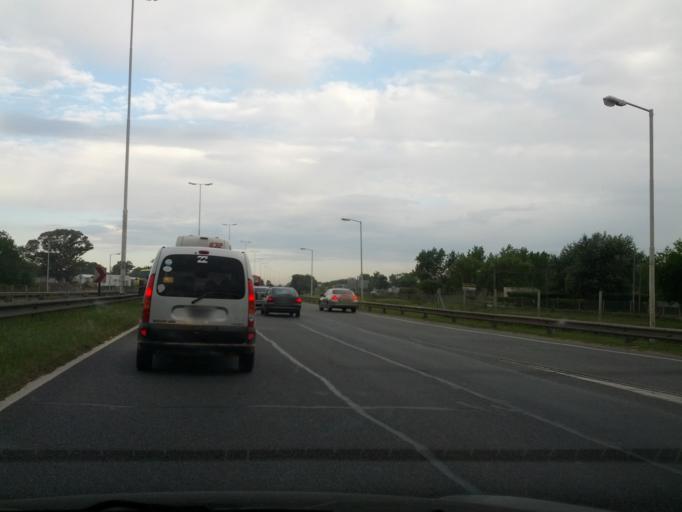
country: AR
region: Buenos Aires
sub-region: Partido de General Rodriguez
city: General Rodriguez
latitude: -34.6026
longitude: -58.8995
